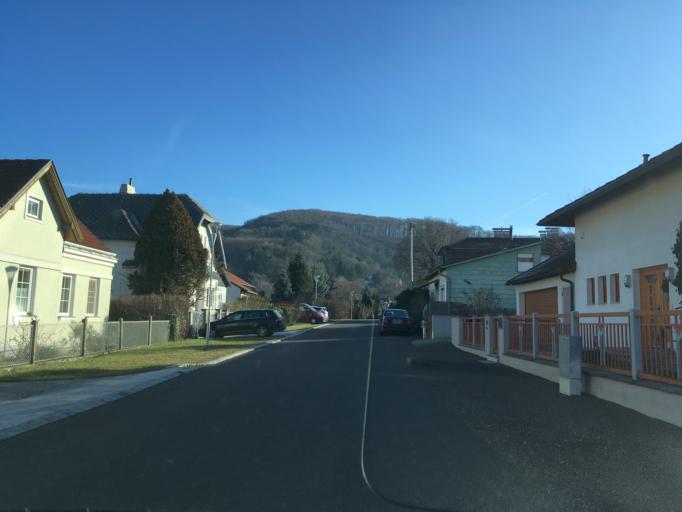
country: AT
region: Lower Austria
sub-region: Politischer Bezirk Tulln
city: Wordern
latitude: 48.3272
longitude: 16.2122
